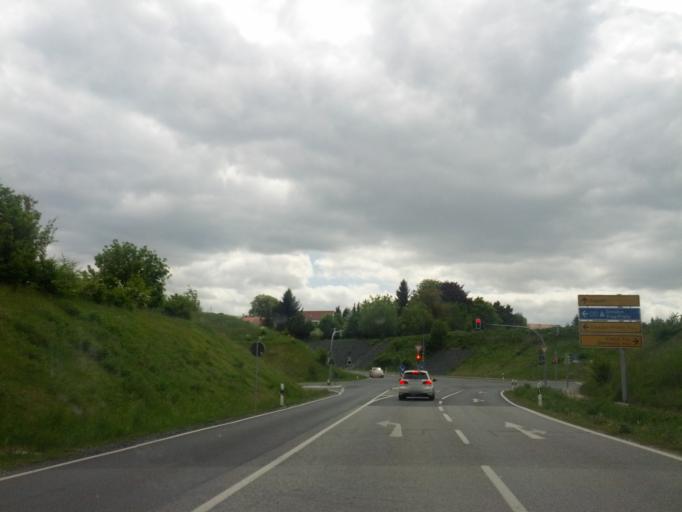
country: DE
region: Saxony
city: Bannewitz
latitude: 50.9927
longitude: 13.7610
